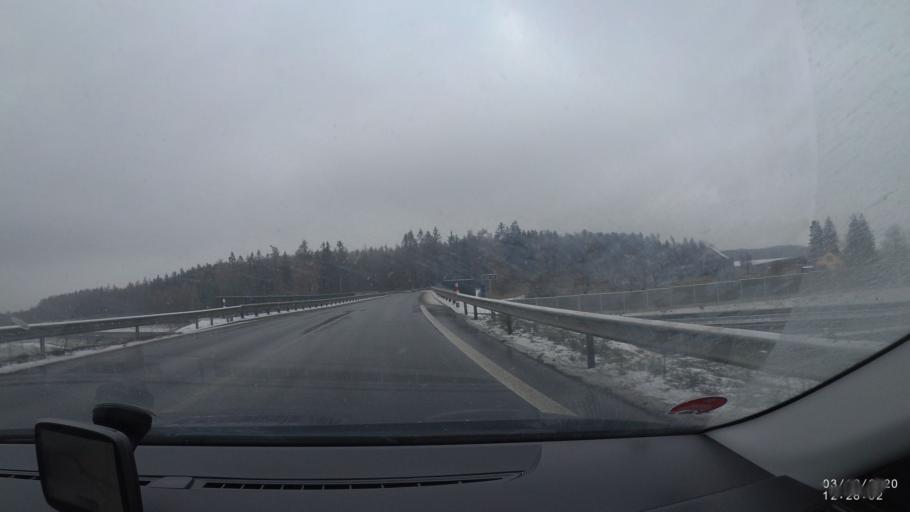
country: CZ
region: Central Bohemia
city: Nove Straseci
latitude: 50.1632
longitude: 13.8830
